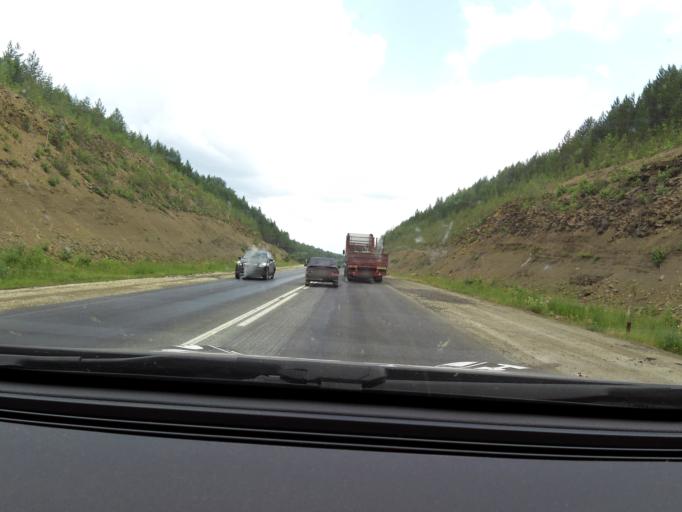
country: RU
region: Sverdlovsk
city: Ufimskiy
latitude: 56.7836
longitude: 58.3065
